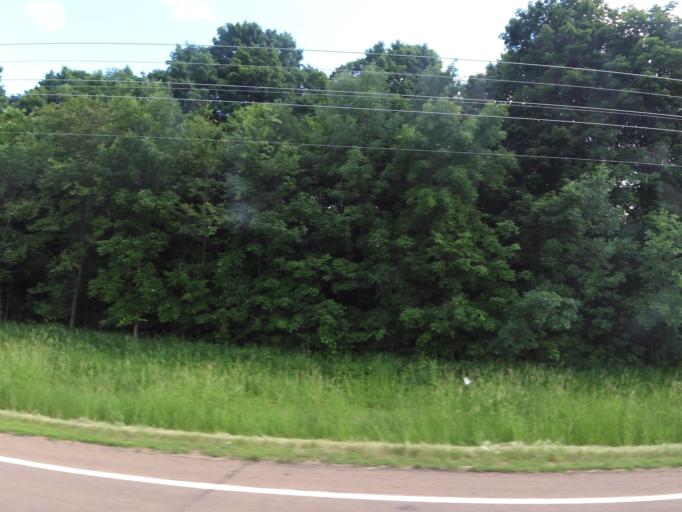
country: US
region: Minnesota
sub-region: Carver County
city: Victoria
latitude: 44.8189
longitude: -93.7179
